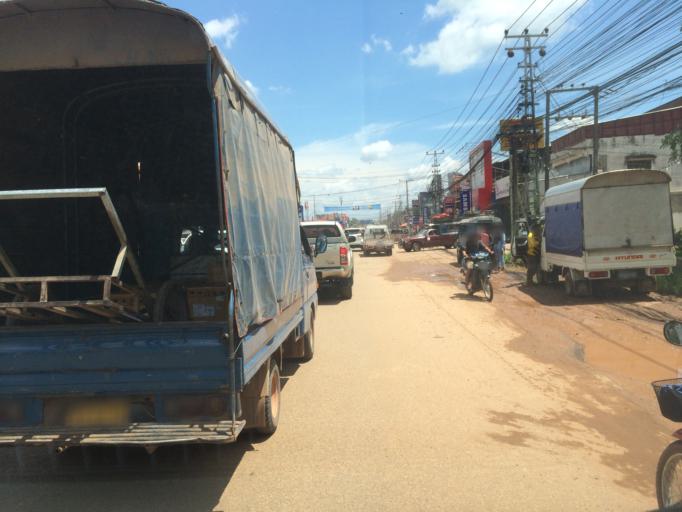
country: TH
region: Nong Khai
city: Si Chiang Mai
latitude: 17.9789
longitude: 102.5552
